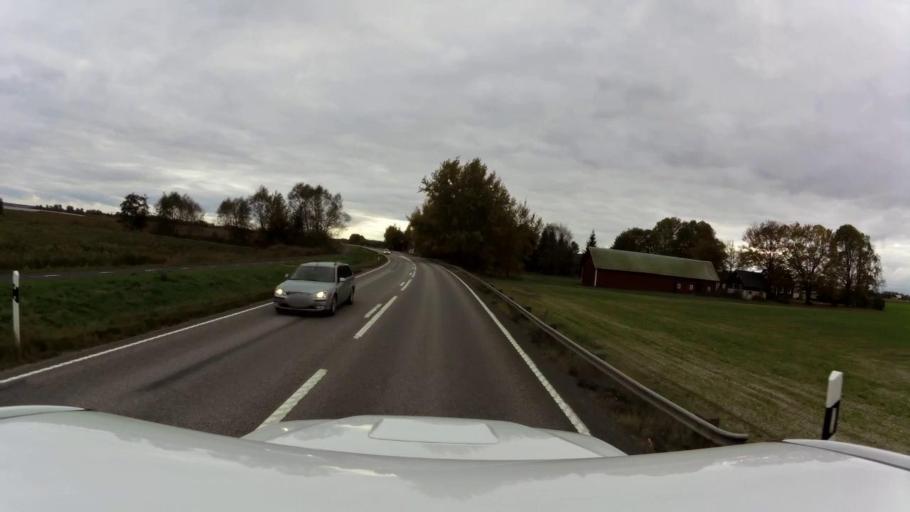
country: SE
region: OEstergoetland
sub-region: Linkopings Kommun
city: Berg
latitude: 58.4696
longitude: 15.5298
